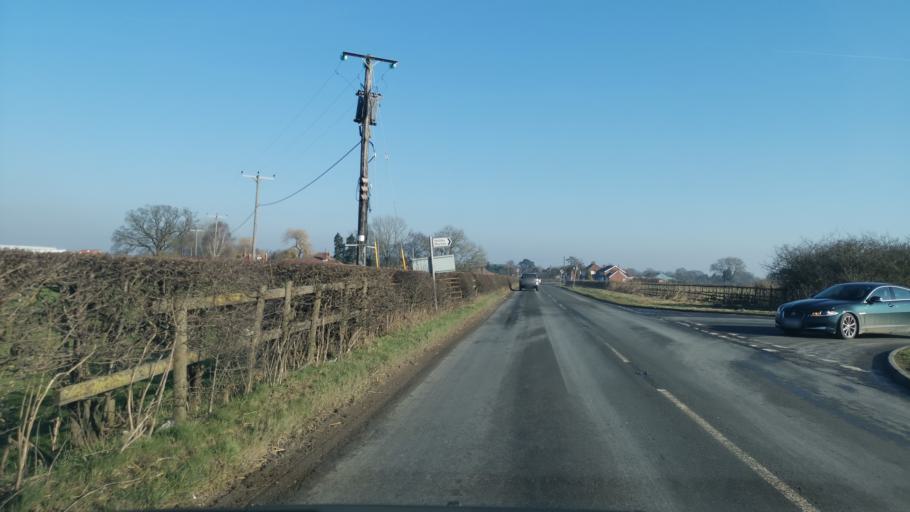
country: GB
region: England
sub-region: City of York
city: Murton
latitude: 53.9870
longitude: -1.0180
